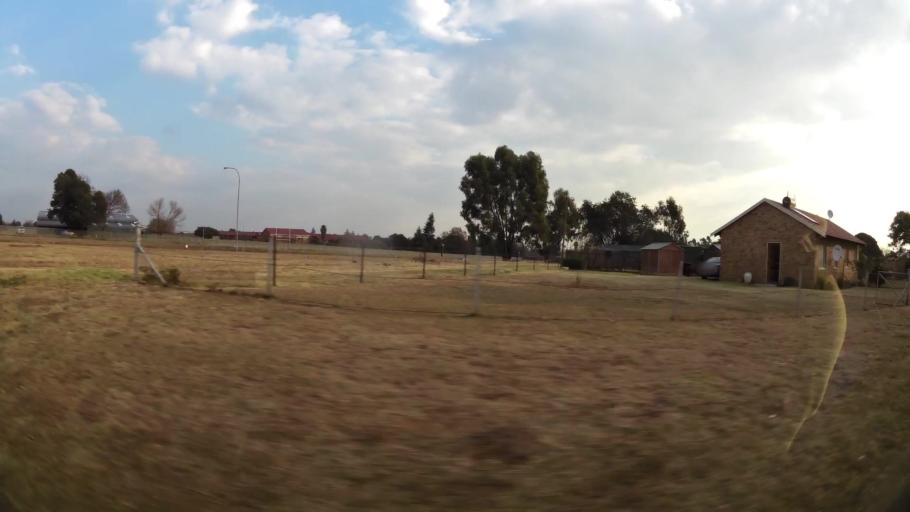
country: ZA
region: Gauteng
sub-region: Ekurhuleni Metropolitan Municipality
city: Benoni
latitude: -26.1596
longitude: 28.3014
